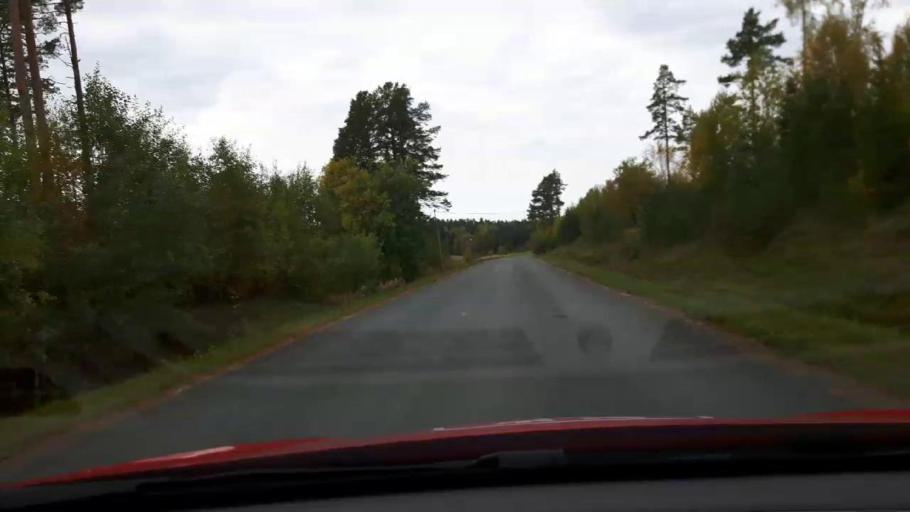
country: SE
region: Jaemtland
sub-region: Krokoms Kommun
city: Krokom
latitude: 63.1989
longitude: 14.1276
